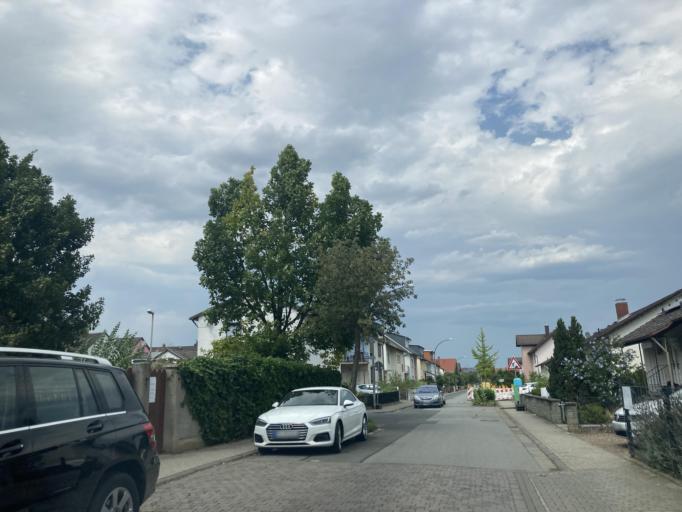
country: DE
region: Hesse
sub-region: Regierungsbezirk Darmstadt
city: Trebur
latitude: 49.9265
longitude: 8.4109
